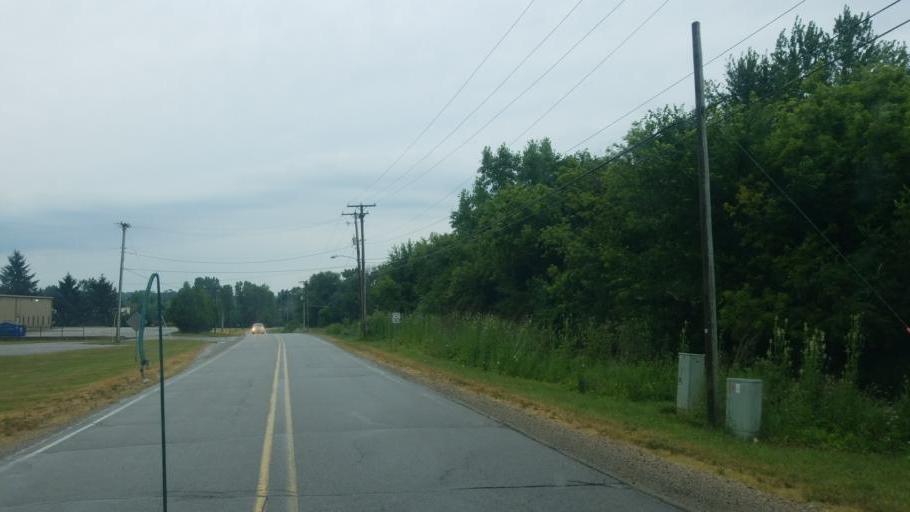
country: US
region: Indiana
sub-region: Steuben County
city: Hamilton
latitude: 41.5373
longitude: -84.9291
